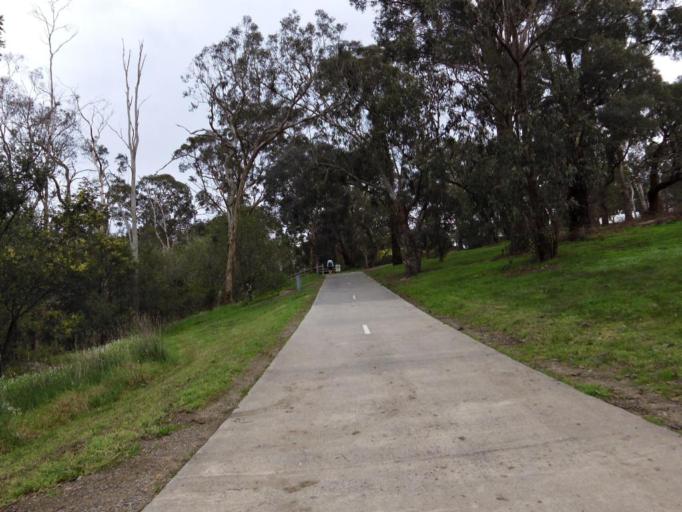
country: AU
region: Victoria
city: Mitcham
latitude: -37.8100
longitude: 145.2115
